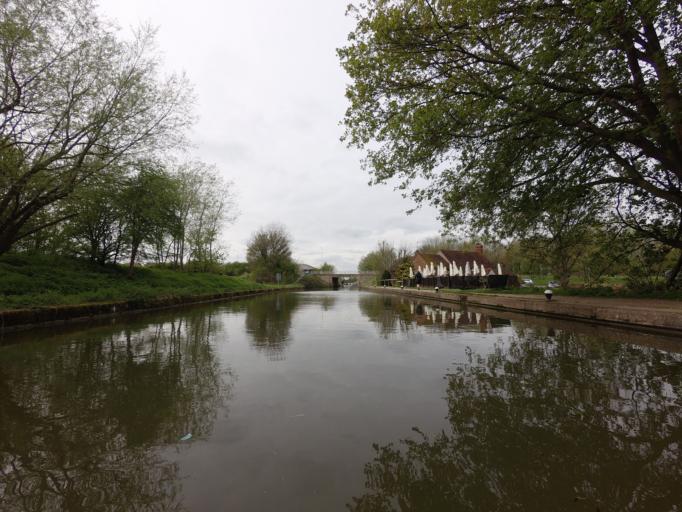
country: GB
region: England
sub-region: Milton Keynes
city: Bradwell
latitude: 52.0726
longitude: -0.7664
